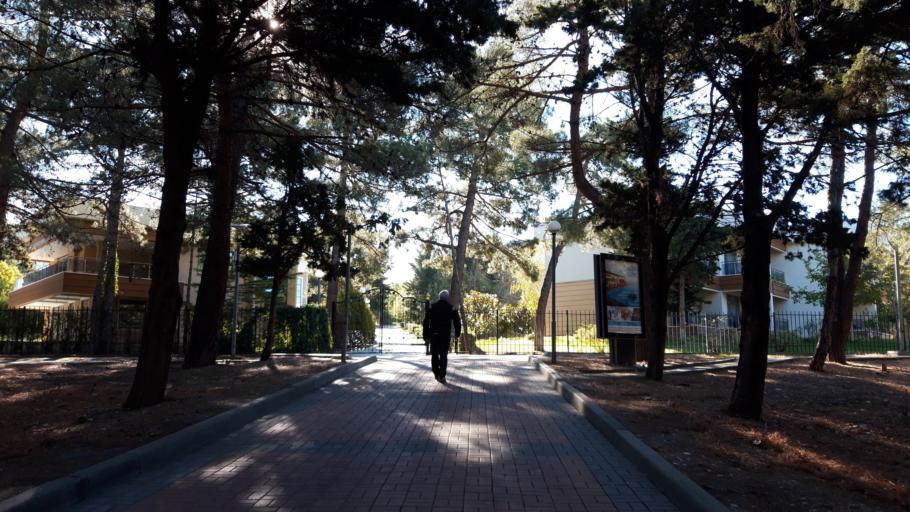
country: RU
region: Krasnodarskiy
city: Gelendzhik
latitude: 44.5537
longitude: 38.0531
